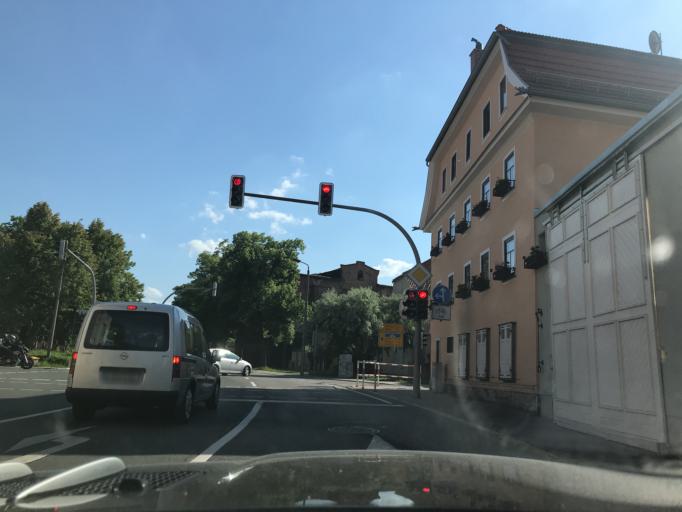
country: DE
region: Thuringia
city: Arnstadt
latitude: 50.8328
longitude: 10.9522
